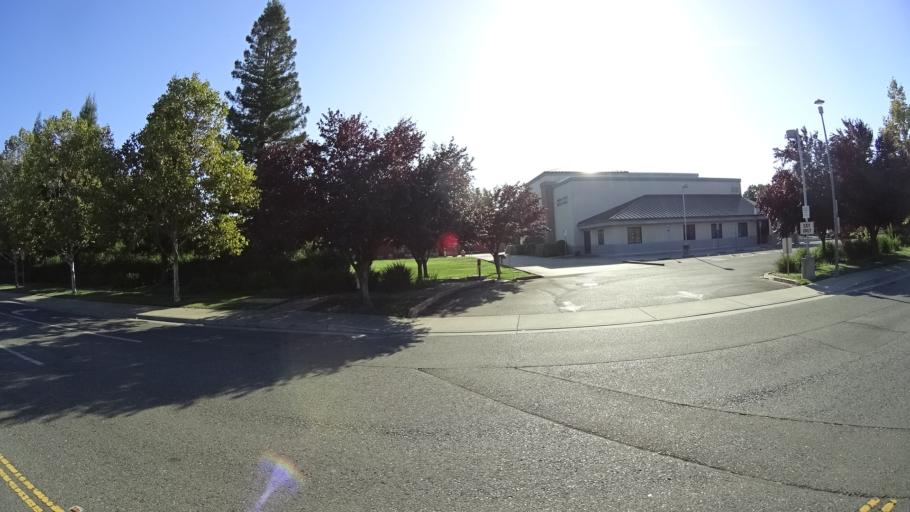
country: US
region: California
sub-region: Sacramento County
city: Laguna
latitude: 38.4226
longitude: -121.4531
